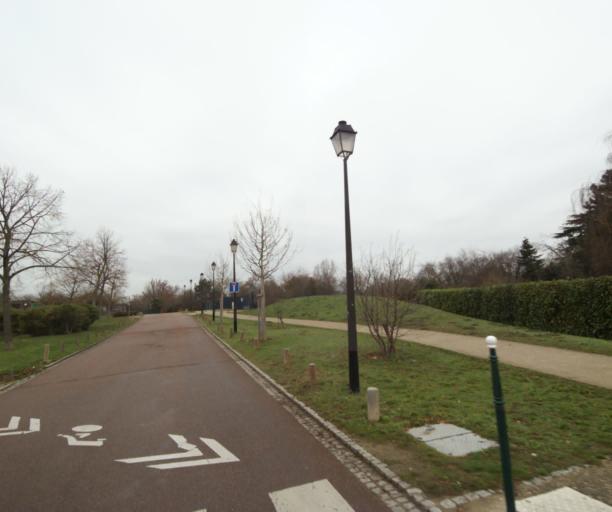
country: FR
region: Ile-de-France
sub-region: Departement des Yvelines
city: Chatou
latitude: 48.8765
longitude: 2.1627
